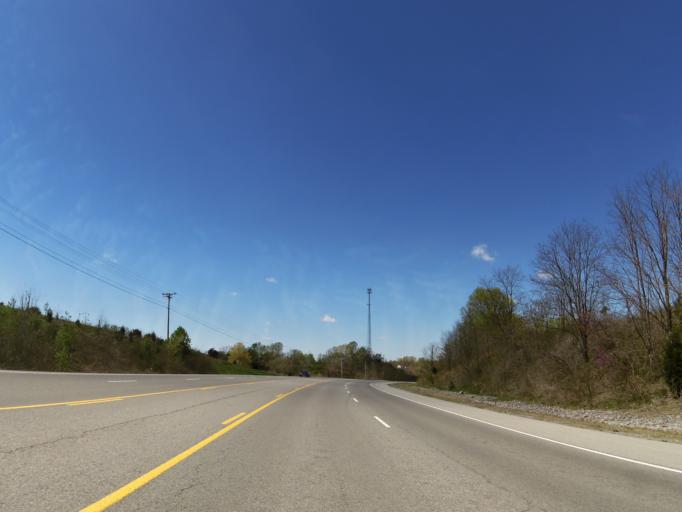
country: US
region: Tennessee
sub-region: DeKalb County
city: Smithville
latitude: 35.9925
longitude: -85.8876
